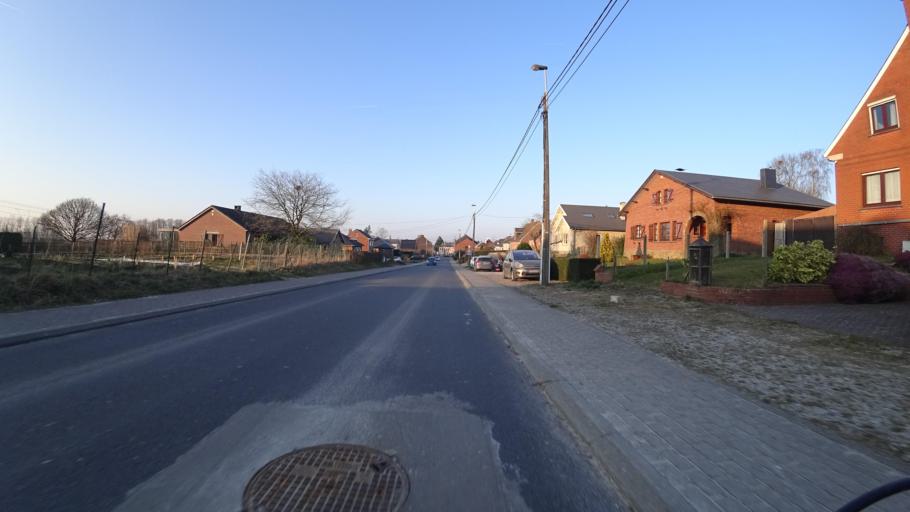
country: BE
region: Wallonia
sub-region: Province du Brabant Wallon
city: Chastre-Villeroux-Blanmont
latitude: 50.6058
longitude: 4.6489
